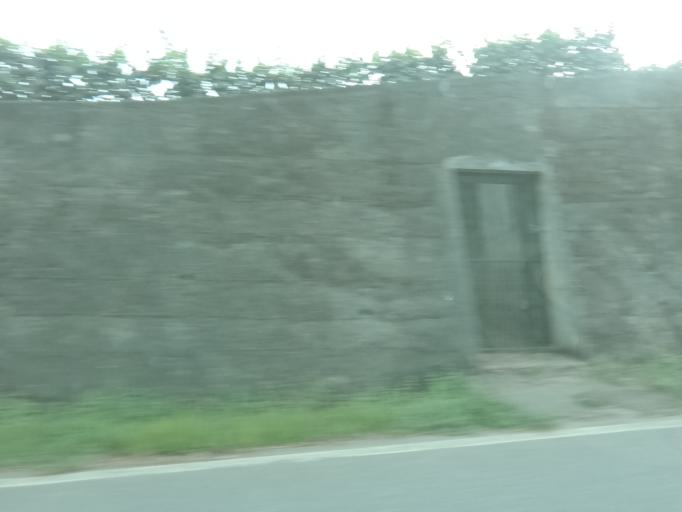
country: PT
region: Vila Real
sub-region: Mesao Frio
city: Mesao Frio
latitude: 41.1848
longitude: -7.8569
